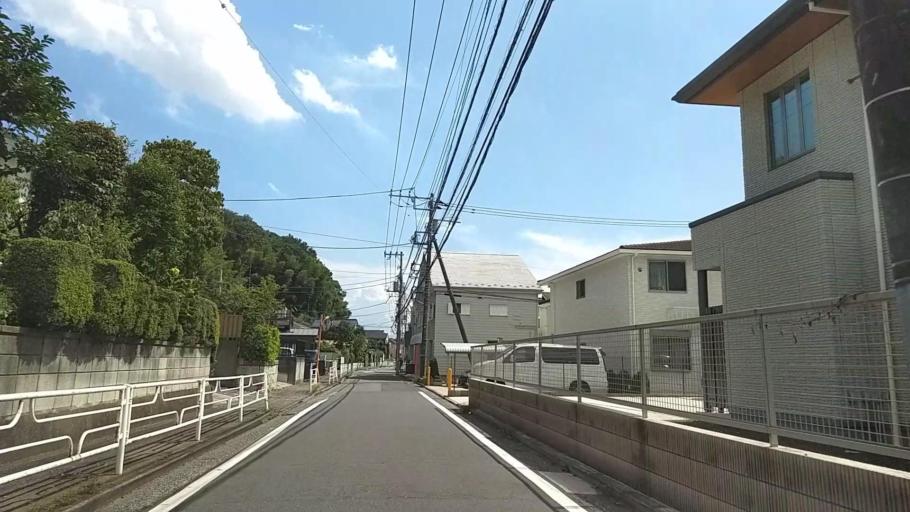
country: JP
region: Kanagawa
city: Yokohama
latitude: 35.5207
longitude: 139.5790
